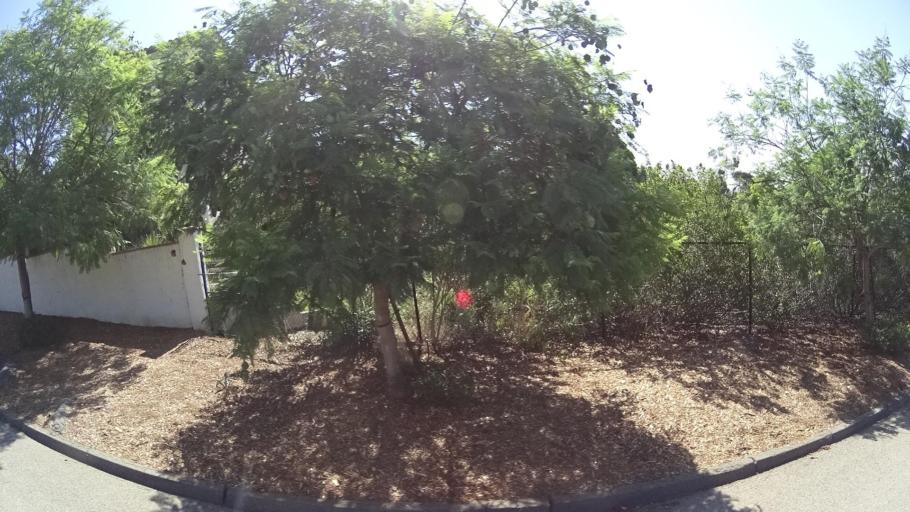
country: US
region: California
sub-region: San Diego County
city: Escondido
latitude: 33.0887
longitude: -117.1095
